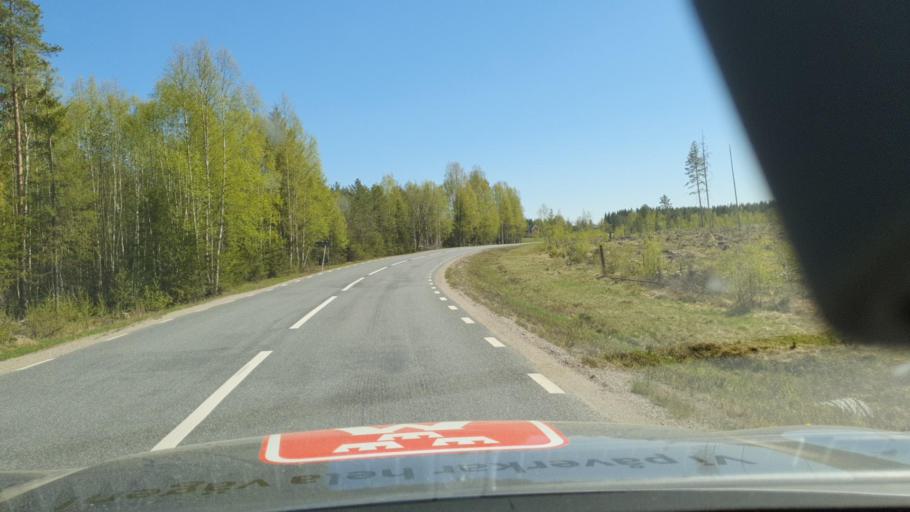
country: SE
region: Vaesternorrland
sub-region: OErnskoeldsviks Kommun
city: Bredbyn
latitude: 63.7492
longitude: 18.4942
